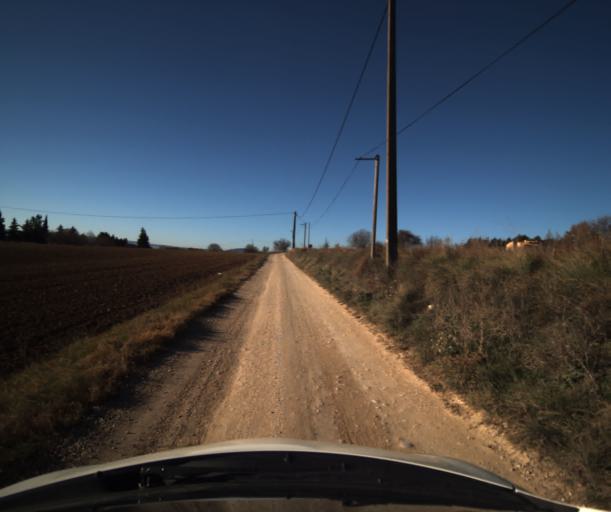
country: FR
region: Provence-Alpes-Cote d'Azur
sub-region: Departement du Vaucluse
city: Pertuis
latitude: 43.7121
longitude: 5.5040
